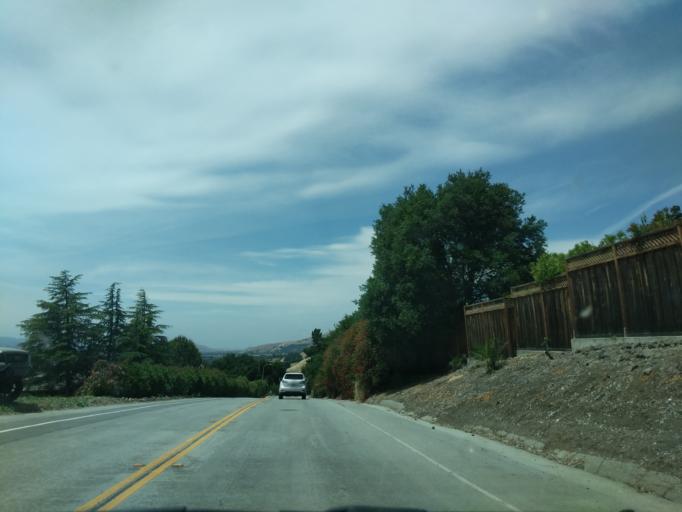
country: US
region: California
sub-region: Santa Clara County
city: San Martin
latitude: 37.1372
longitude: -121.5977
